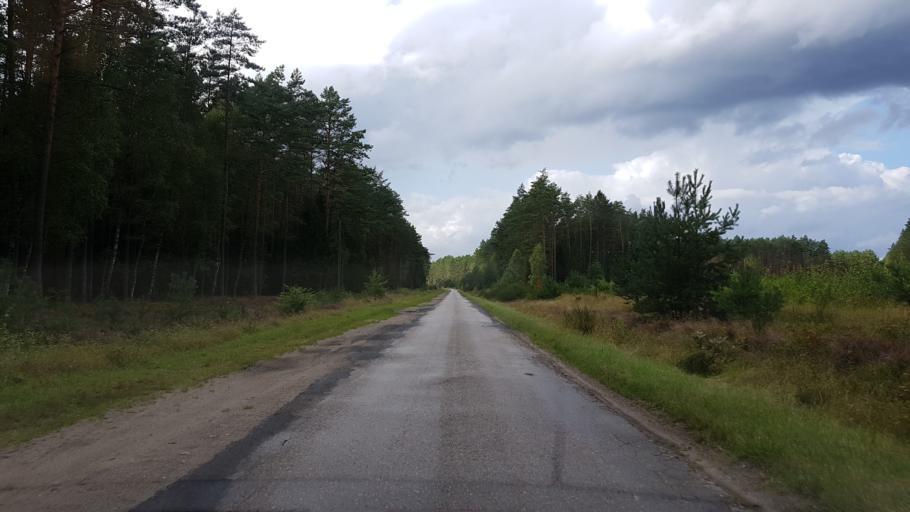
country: PL
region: West Pomeranian Voivodeship
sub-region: Powiat bialogardzki
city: Tychowo
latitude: 54.0377
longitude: 16.3335
